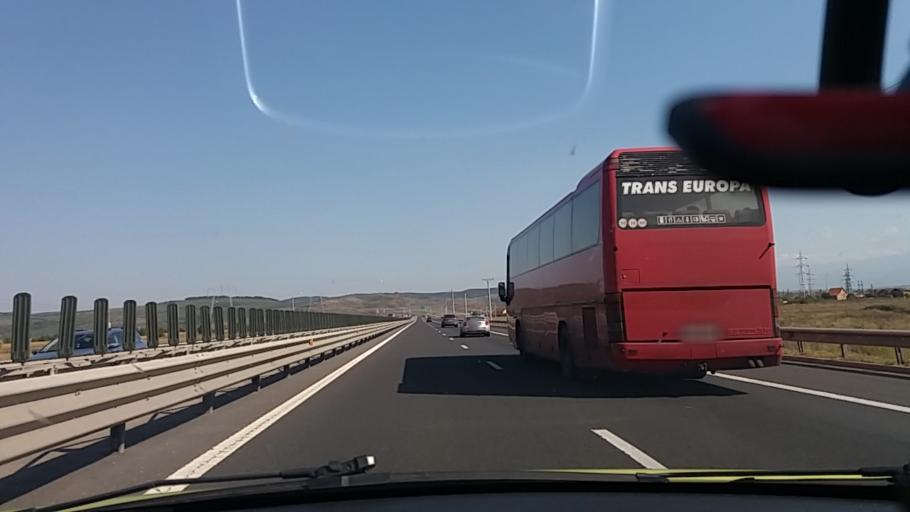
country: RO
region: Sibiu
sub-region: Municipiul Sibiu
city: Sibiu
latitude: 45.8250
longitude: 24.1335
